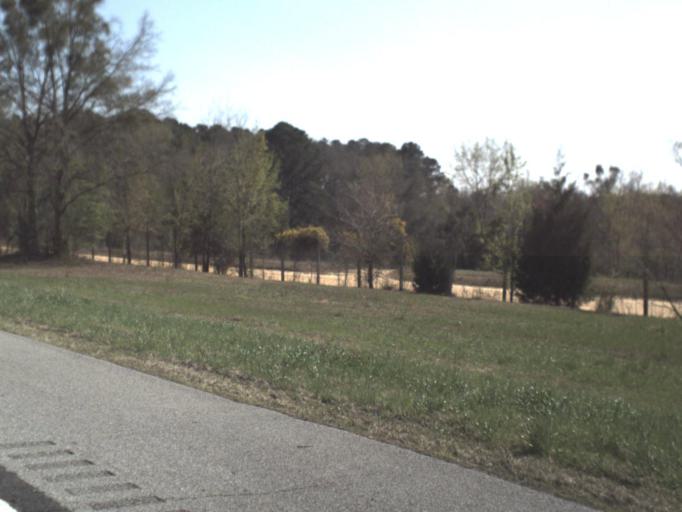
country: US
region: Florida
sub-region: Jackson County
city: Sneads
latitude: 30.6451
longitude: -85.0079
